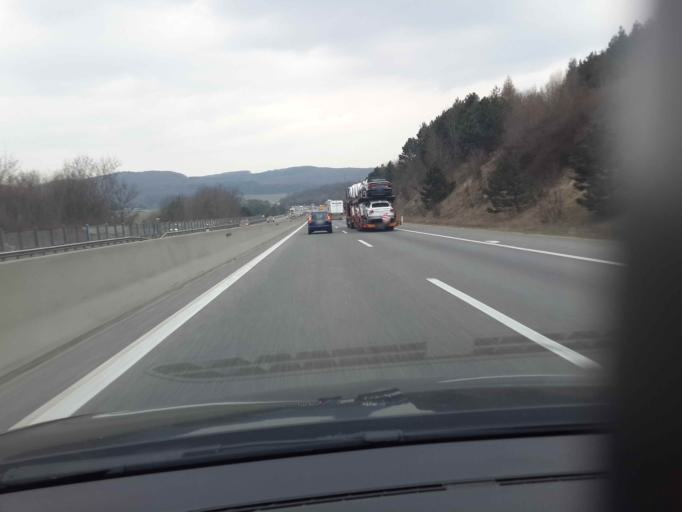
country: AT
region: Lower Austria
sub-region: Politischer Bezirk Baden
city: Heiligenkreuz
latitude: 48.0618
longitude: 16.1337
